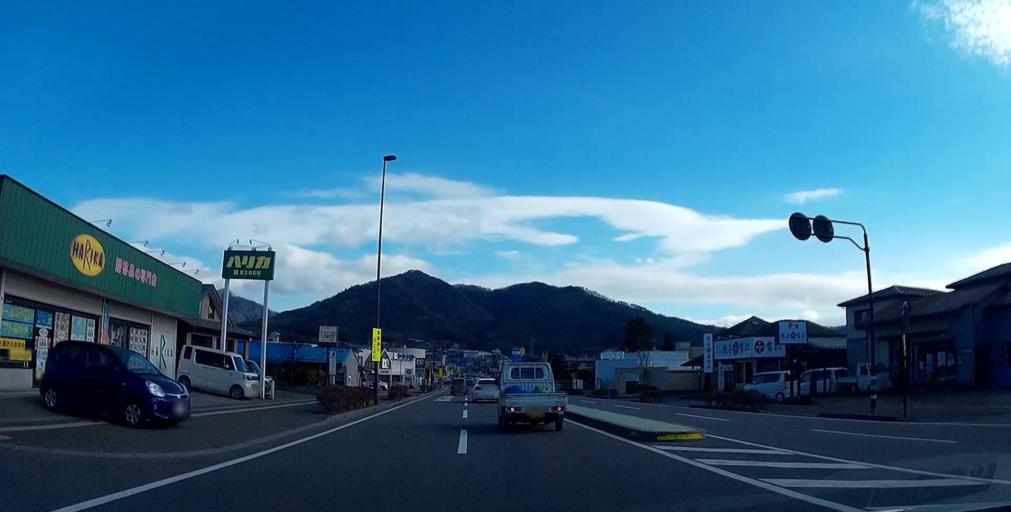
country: JP
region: Yamanashi
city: Fujikawaguchiko
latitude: 35.4830
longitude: 138.8073
